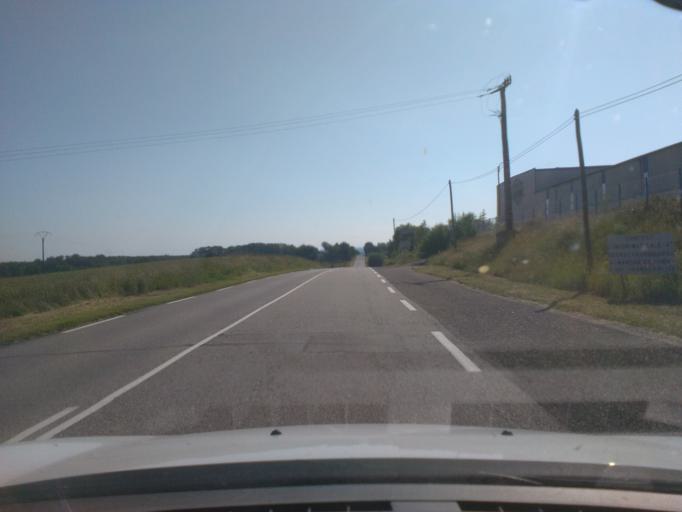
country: FR
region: Lorraine
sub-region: Departement des Vosges
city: Aydoilles
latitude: 48.2094
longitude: 6.5570
